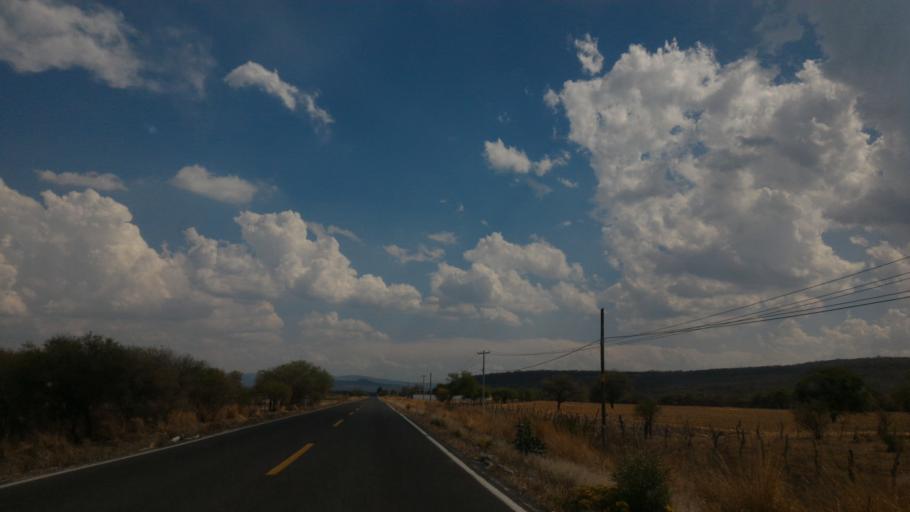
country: MX
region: Guanajuato
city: Ciudad Manuel Doblado
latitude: 20.7699
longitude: -101.9728
